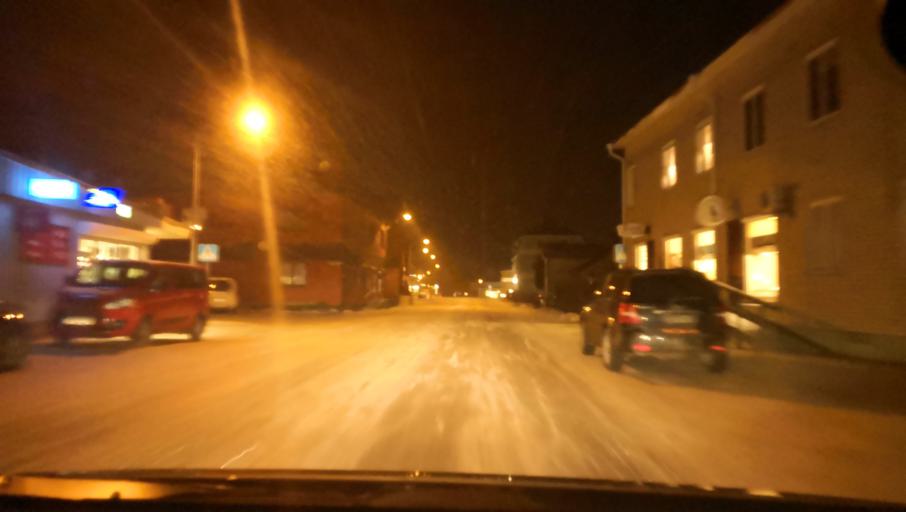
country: SE
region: Uppsala
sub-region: Heby Kommun
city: Tarnsjo
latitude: 60.1547
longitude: 16.9298
